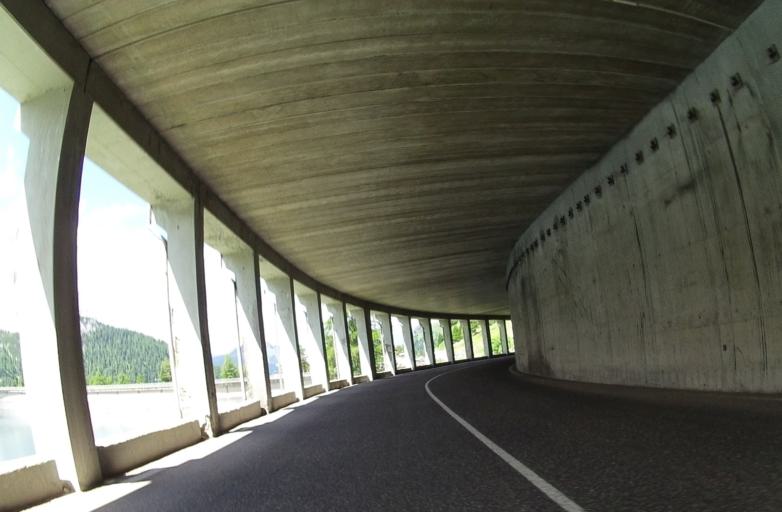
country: IT
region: Trentino-Alto Adige
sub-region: Bolzano
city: Corvara in Badia
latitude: 46.4635
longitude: 11.8652
